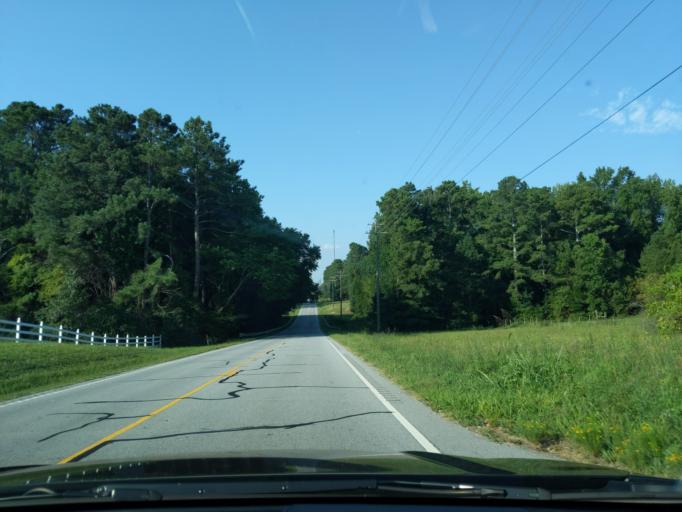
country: US
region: South Carolina
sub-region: Newberry County
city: Newberry
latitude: 34.2975
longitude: -81.5909
